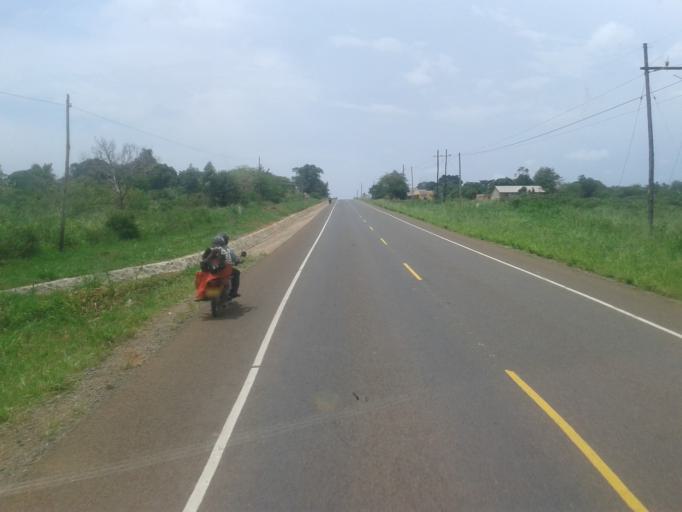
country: UG
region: Western Region
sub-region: Kiryandongo District
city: Kiryandongo
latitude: 1.8825
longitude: 32.0662
